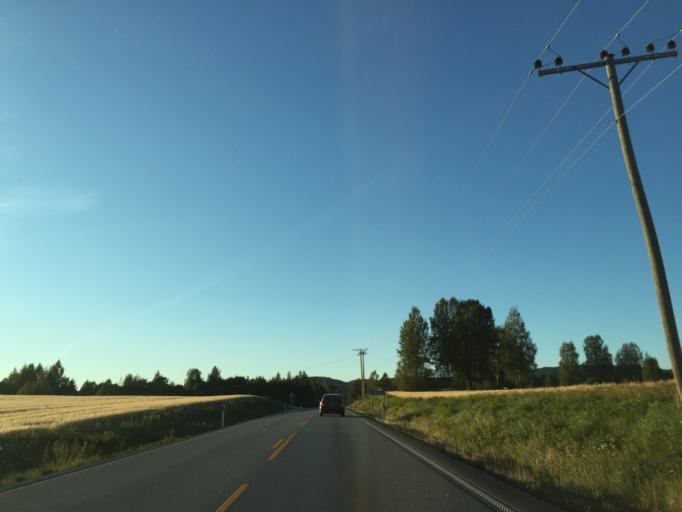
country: NO
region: Hedmark
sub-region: Nord-Odal
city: Sand
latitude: 60.4375
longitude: 11.5065
